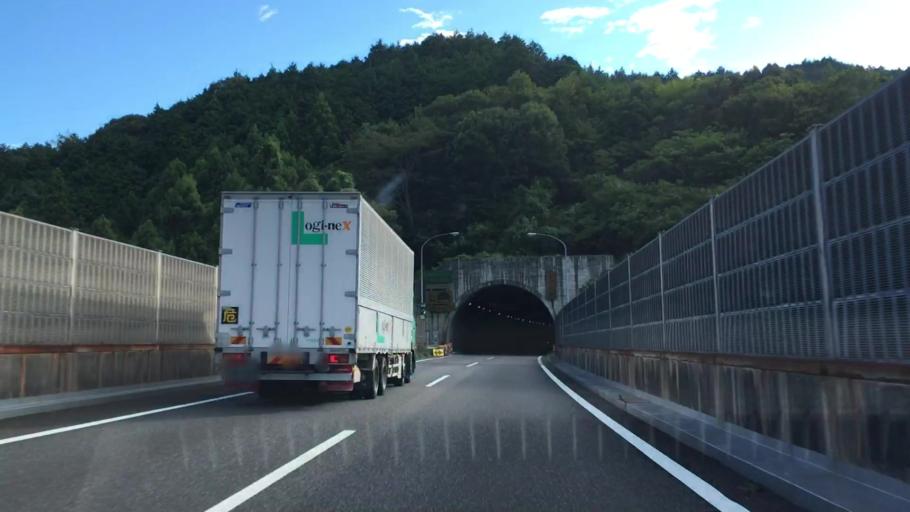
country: JP
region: Yamaguchi
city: Iwakuni
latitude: 34.1569
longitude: 132.1501
